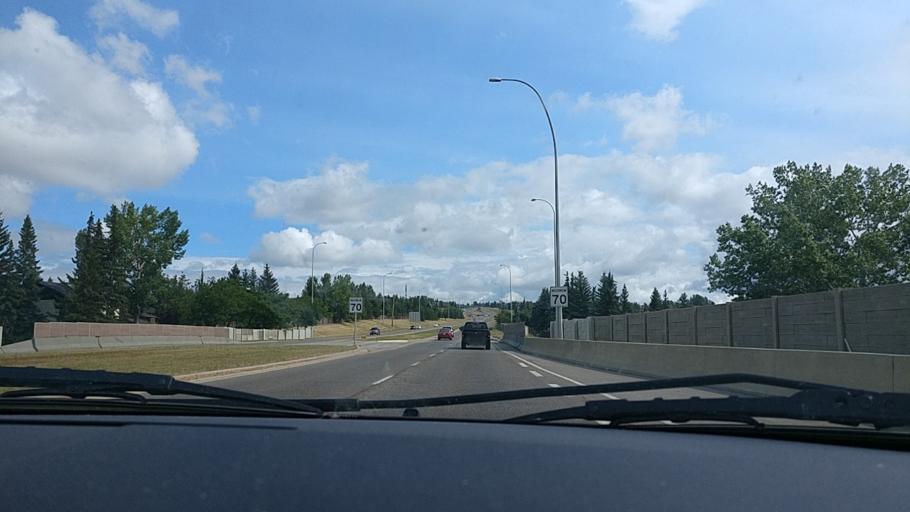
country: CA
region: Alberta
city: Calgary
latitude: 51.1146
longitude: -114.1744
